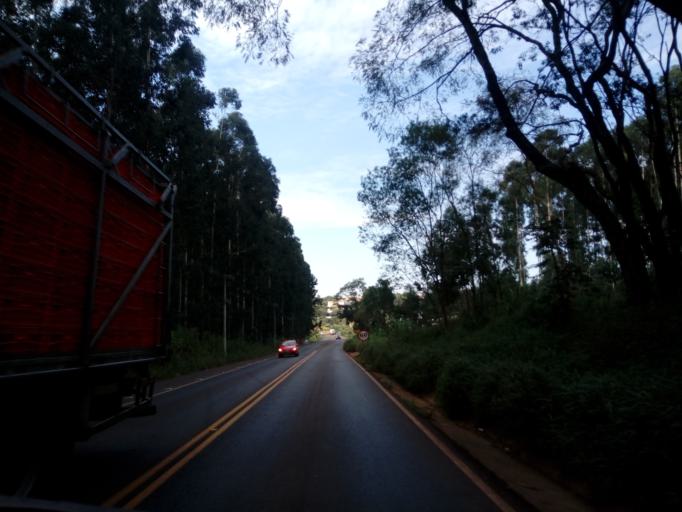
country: BR
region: Santa Catarina
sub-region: Chapeco
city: Chapeco
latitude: -27.0944
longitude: -52.7111
